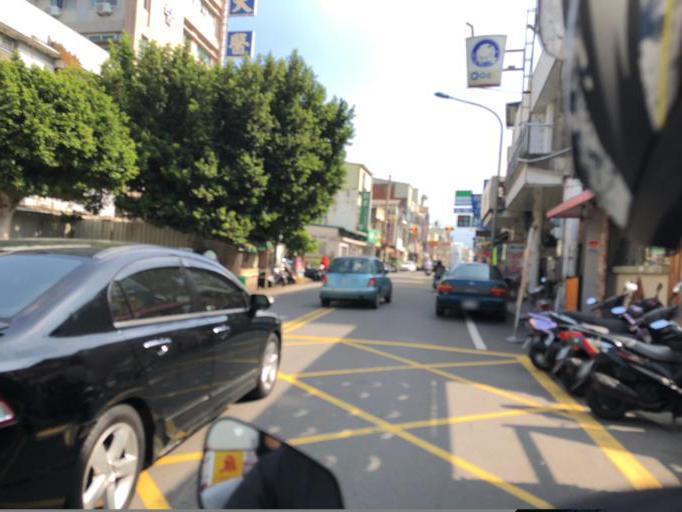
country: TW
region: Taiwan
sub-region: Miaoli
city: Miaoli
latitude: 24.5515
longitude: 120.8206
